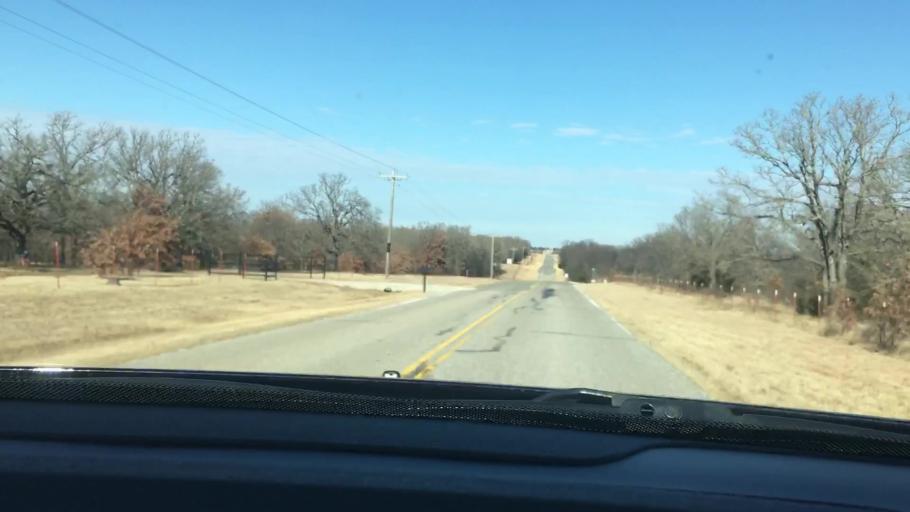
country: US
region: Oklahoma
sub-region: Garvin County
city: Wynnewood
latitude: 34.6644
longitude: -97.1254
